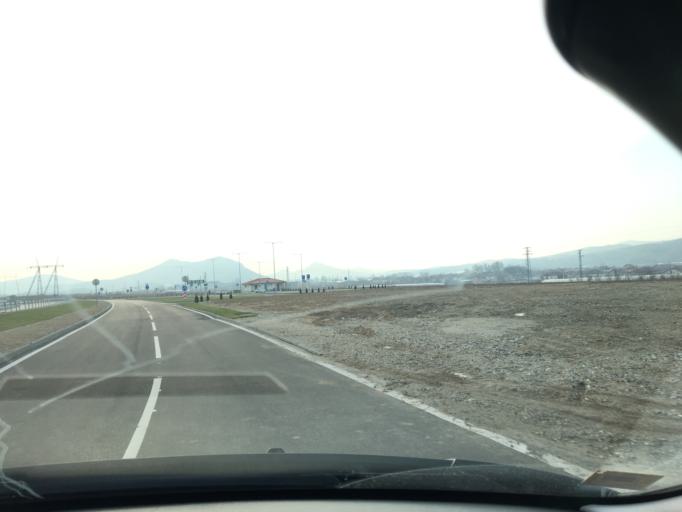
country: BG
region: Blagoevgrad
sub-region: Obshtina Sandanski
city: Sandanski
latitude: 41.5140
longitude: 23.2713
